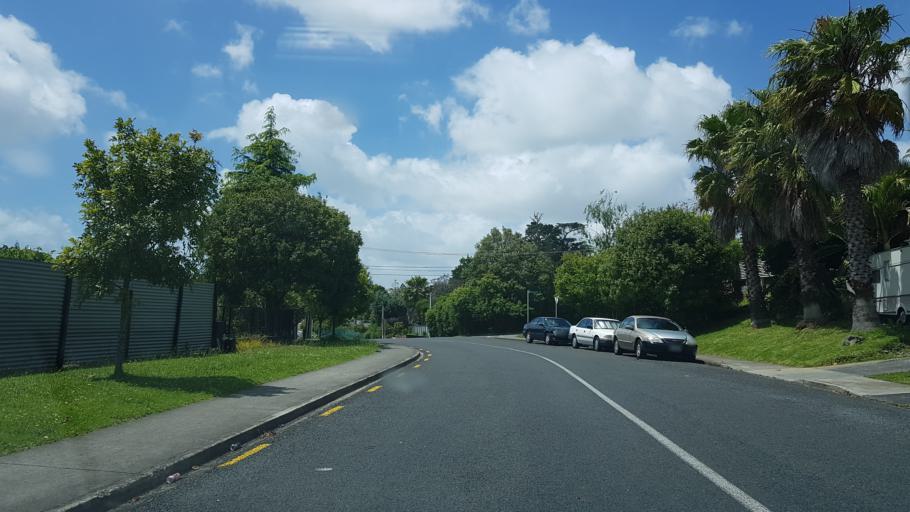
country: NZ
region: Auckland
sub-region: Auckland
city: North Shore
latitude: -36.7906
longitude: 174.7040
